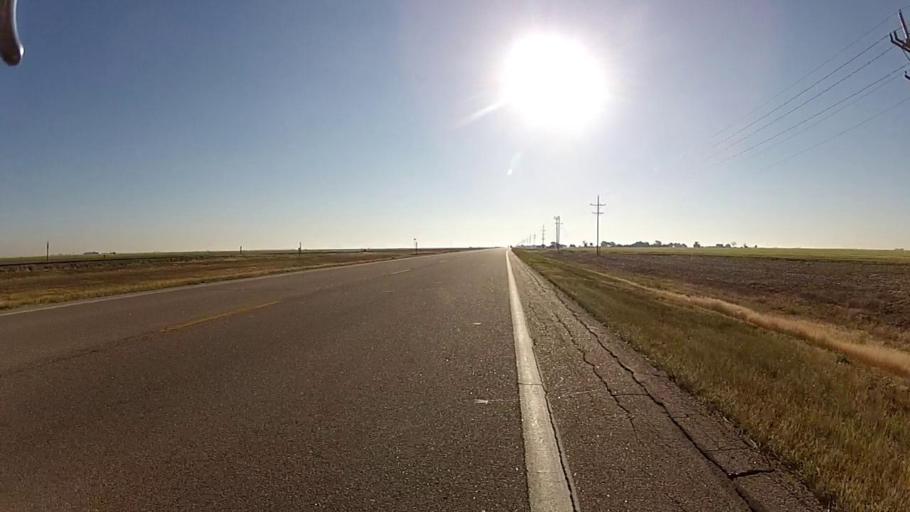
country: US
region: Kansas
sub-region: Haskell County
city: Sublette
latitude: 37.4887
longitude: -100.8246
